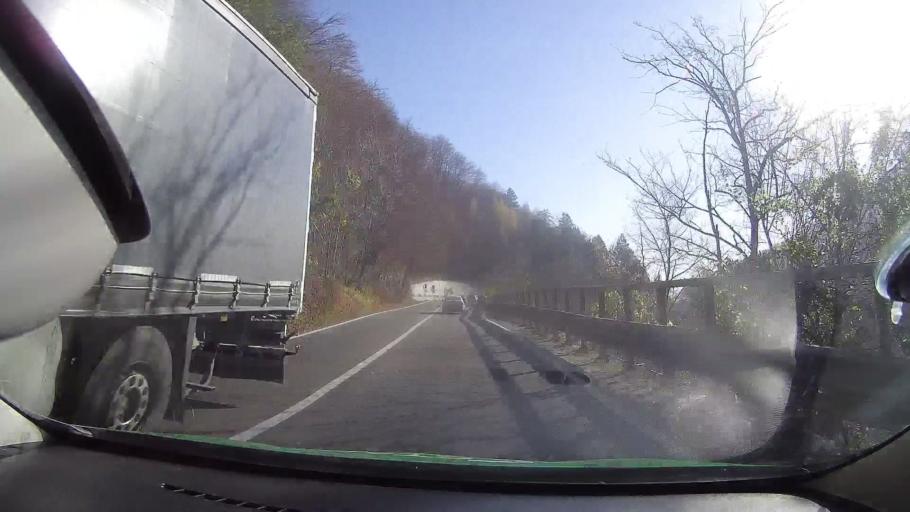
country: RO
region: Prahova
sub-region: Comuna Comarnic
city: Posada
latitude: 45.2970
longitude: 25.5958
